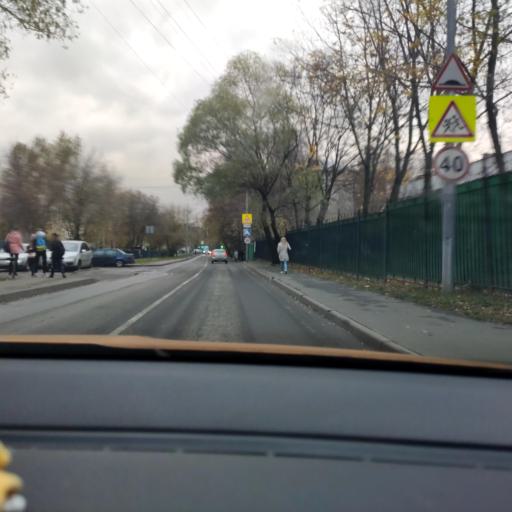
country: RU
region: Moscow
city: Yaroslavskiy
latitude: 55.8753
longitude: 37.7096
